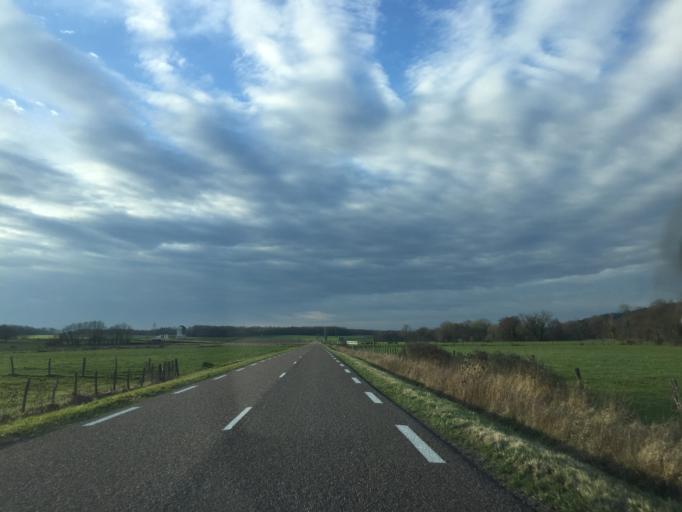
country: FR
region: Franche-Comte
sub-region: Departement du Jura
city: Arbois
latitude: 46.9211
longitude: 5.7117
